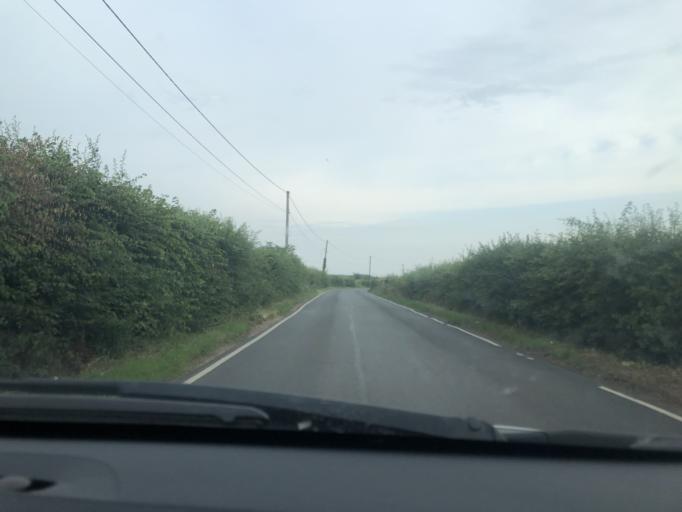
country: GB
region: England
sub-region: Kent
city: Sturry
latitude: 51.3244
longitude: 1.1433
